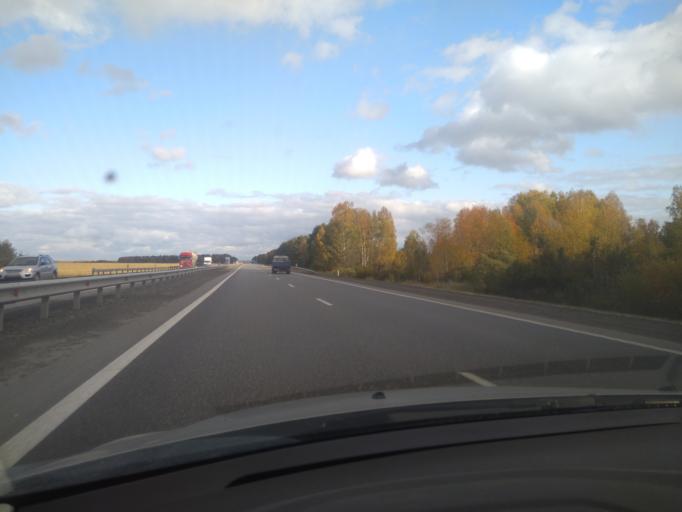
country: RU
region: Tjumen
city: Moskovskiy
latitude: 57.0968
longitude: 65.2449
